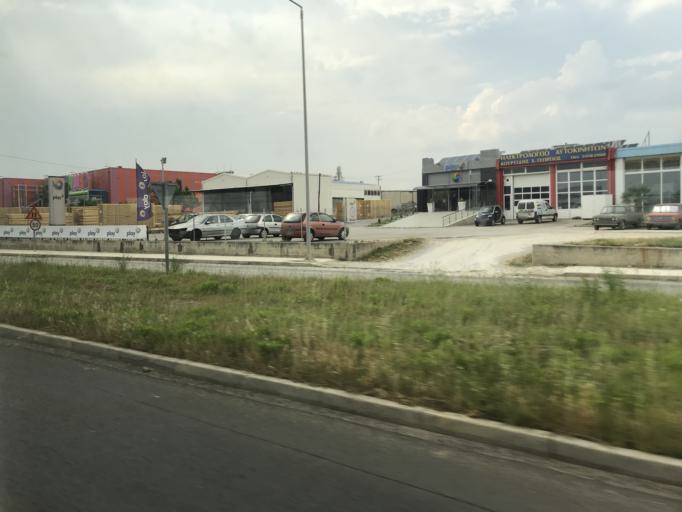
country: GR
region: East Macedonia and Thrace
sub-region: Nomos Evrou
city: Alexandroupoli
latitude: 40.8542
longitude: 25.9166
